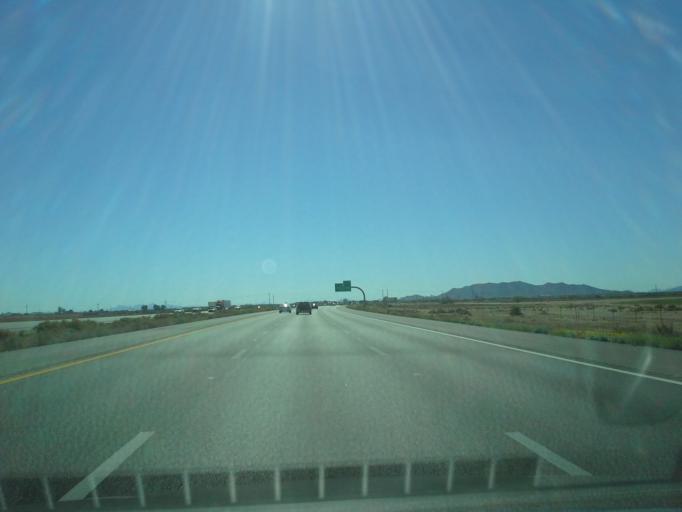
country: US
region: Arizona
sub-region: Pinal County
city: Casa Grande
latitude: 32.9142
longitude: -111.6871
